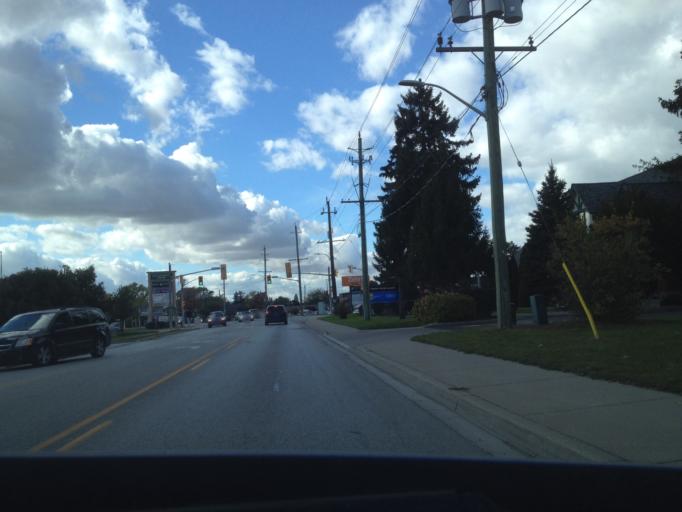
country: CA
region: Ontario
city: Amherstburg
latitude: 42.0382
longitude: -82.7239
